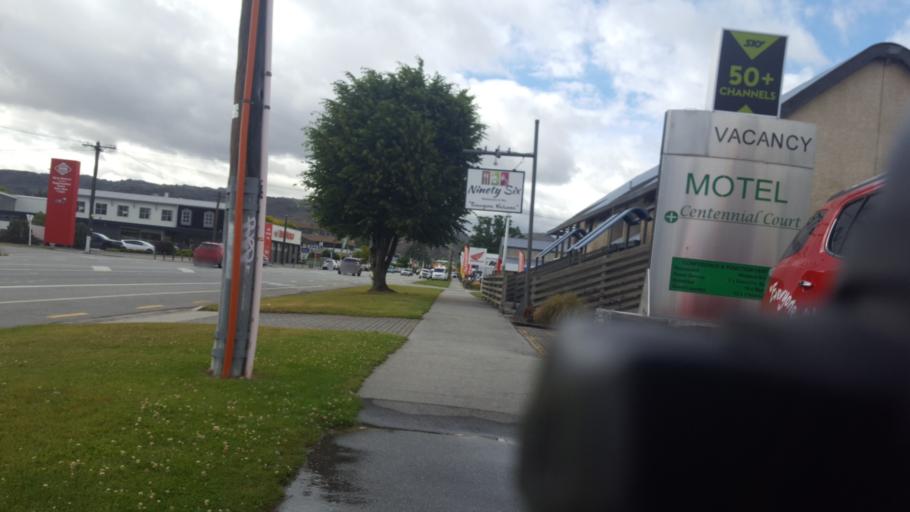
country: NZ
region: Otago
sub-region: Queenstown-Lakes District
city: Wanaka
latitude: -45.2495
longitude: 169.3858
